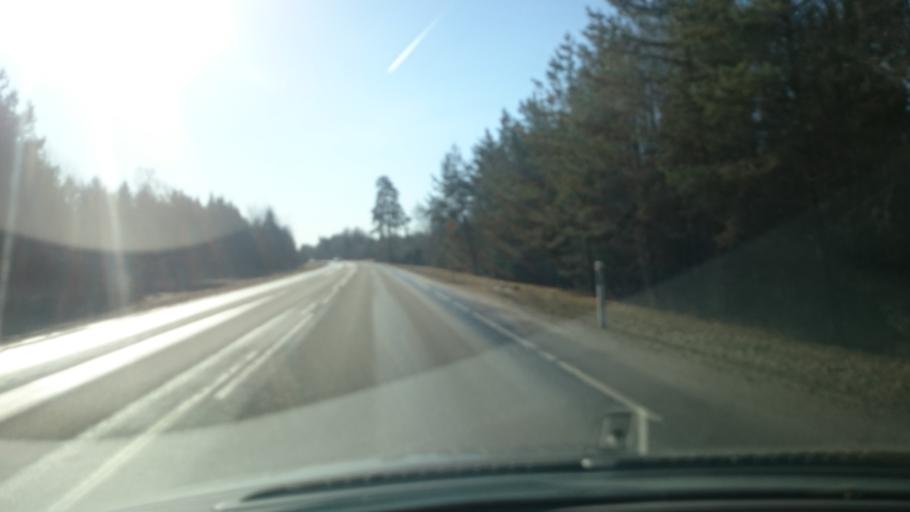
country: EE
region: Raplamaa
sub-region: Kohila vald
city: Kohila
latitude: 59.2441
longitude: 24.7511
